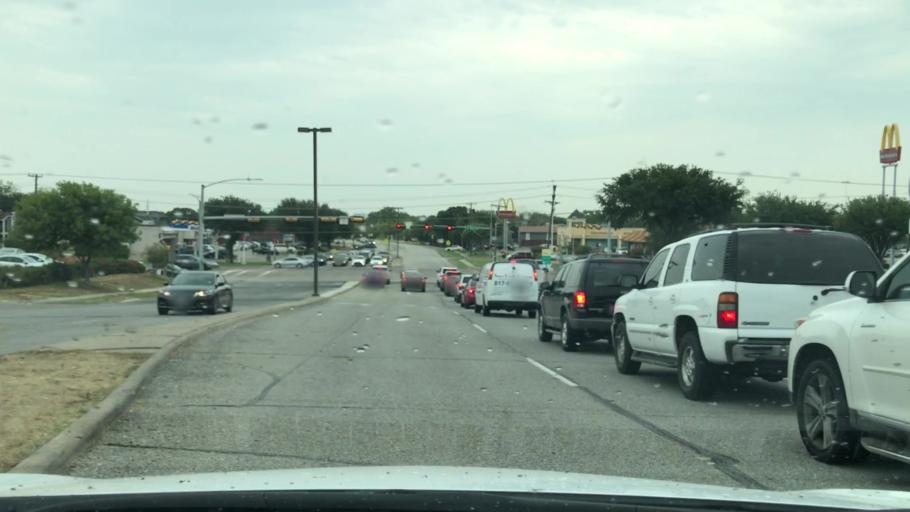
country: US
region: Texas
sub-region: Dallas County
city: Irving
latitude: 32.8652
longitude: -96.9928
